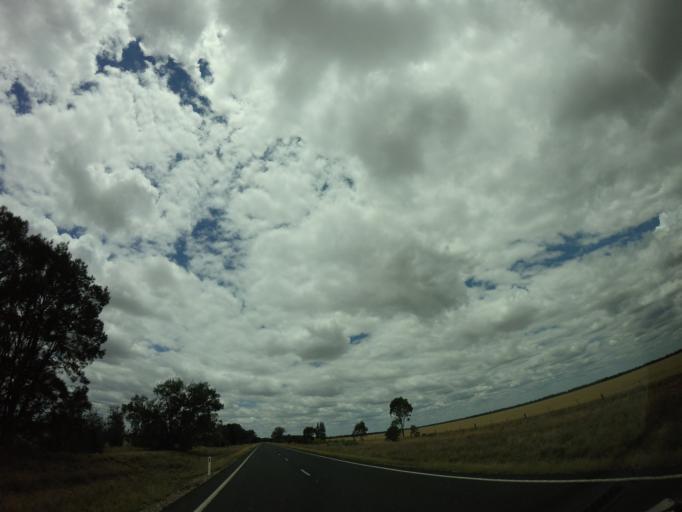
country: AU
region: Queensland
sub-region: Goondiwindi
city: Goondiwindi
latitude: -28.1659
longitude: 150.5297
